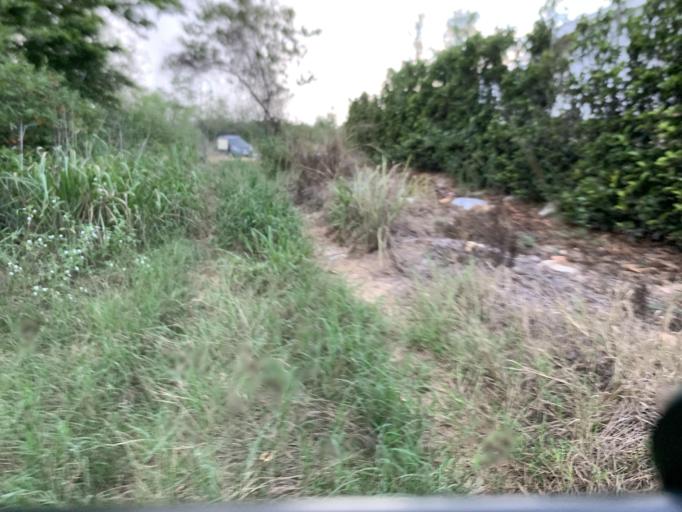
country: MX
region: Nuevo Leon
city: Santiago
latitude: 25.5091
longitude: -100.1811
